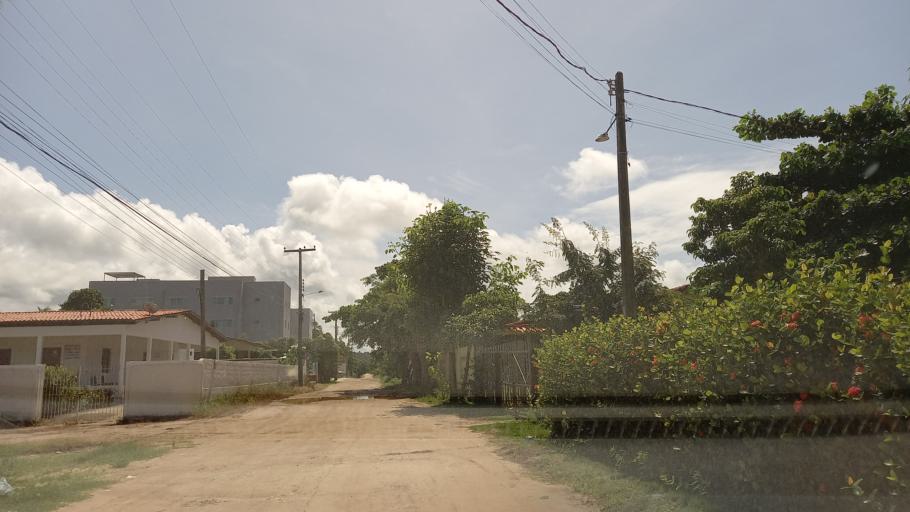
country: BR
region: Pernambuco
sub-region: Sao Jose Da Coroa Grande
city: Sao Jose da Coroa Grande
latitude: -8.9238
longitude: -35.1622
